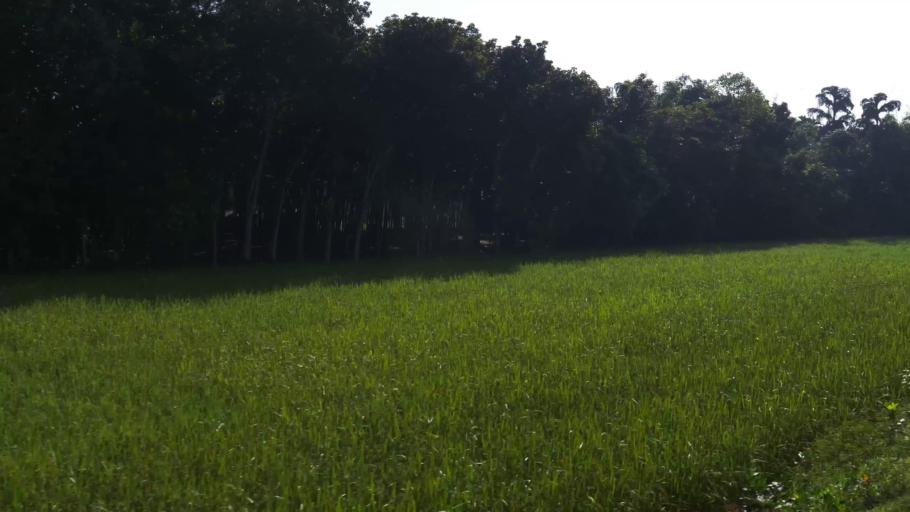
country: BD
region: Dhaka
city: Muktagacha
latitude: 24.8012
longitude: 90.3082
